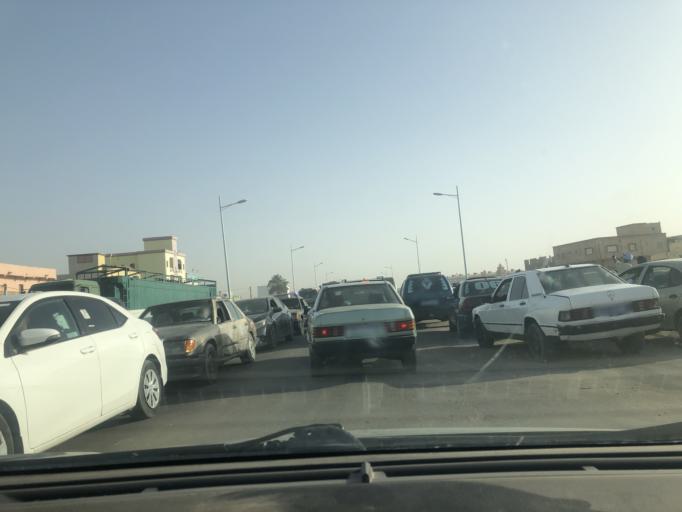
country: MR
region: Nouakchott
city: Nouakchott
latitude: 18.0781
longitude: -15.9657
